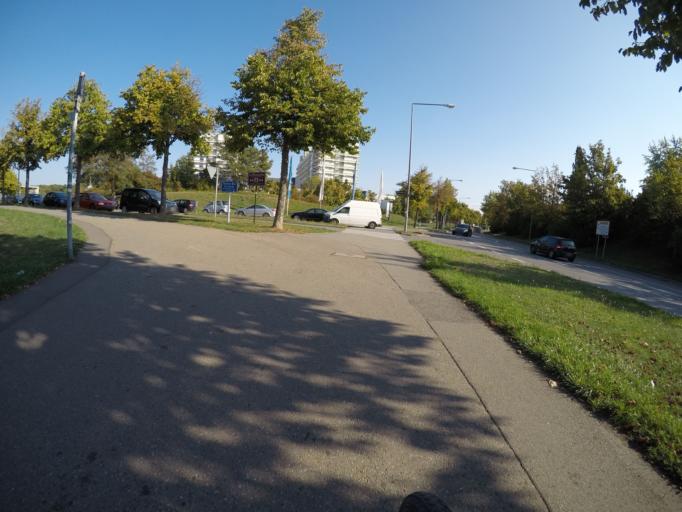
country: DE
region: Baden-Wuerttemberg
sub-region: Regierungsbezirk Stuttgart
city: Gerlingen
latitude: 48.7430
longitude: 9.1037
